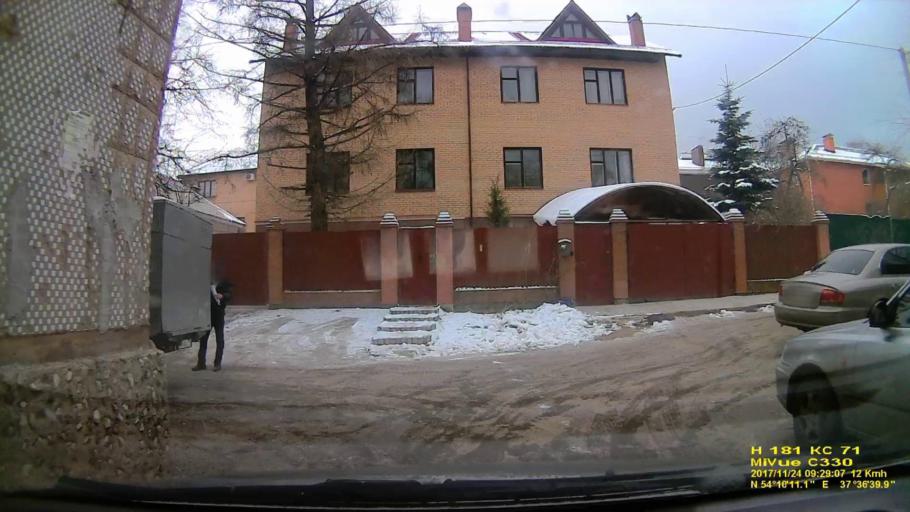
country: RU
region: Tula
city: Tula
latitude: 54.1701
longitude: 37.6112
